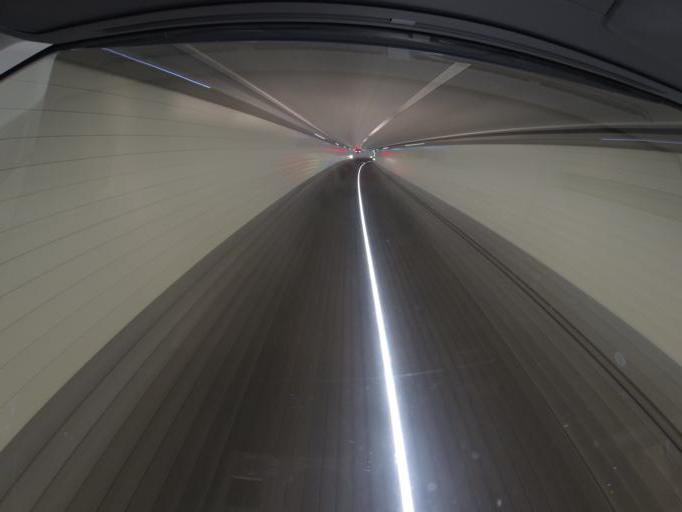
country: CH
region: Saint Gallen
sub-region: Wahlkreis Sarganserland
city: Quarten
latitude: 47.1120
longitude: 9.2086
